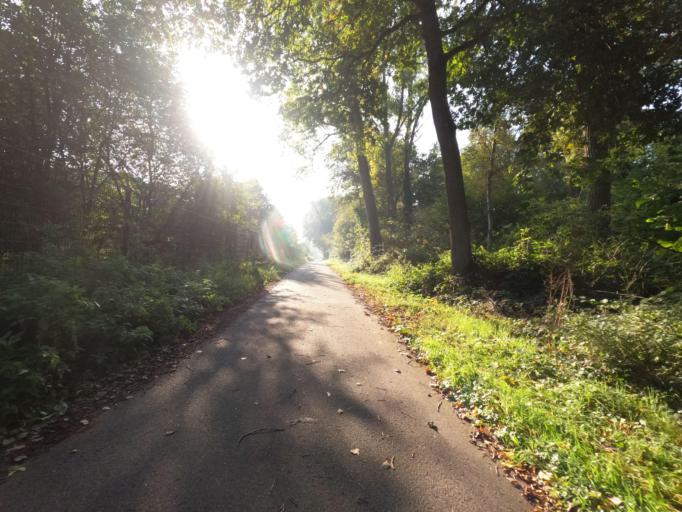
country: DE
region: North Rhine-Westphalia
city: Huckelhoven
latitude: 51.0372
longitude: 6.2494
